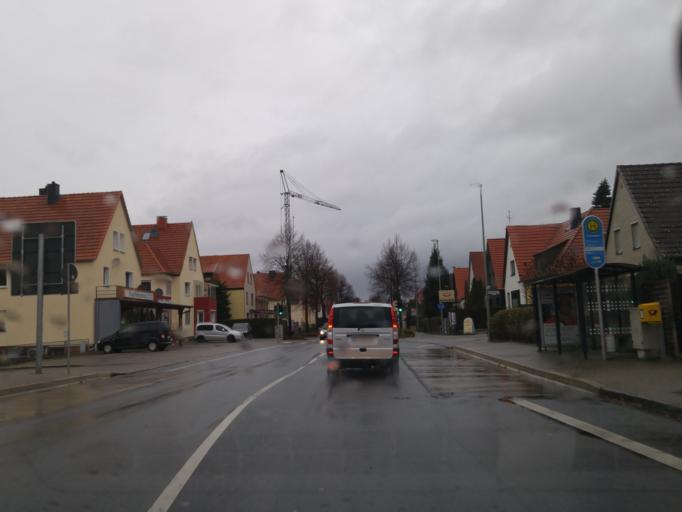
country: DE
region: Lower Saxony
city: Goettingen
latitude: 51.5147
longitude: 9.9399
